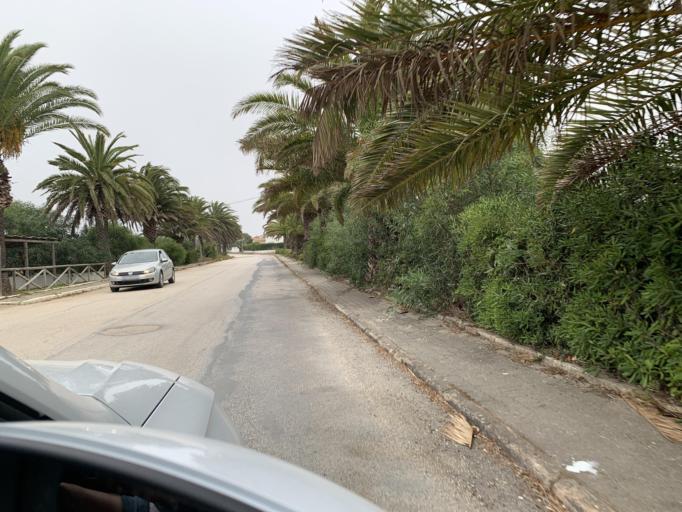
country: PT
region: Faro
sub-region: Aljezur
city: Aljezur
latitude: 37.3031
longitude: -8.8496
